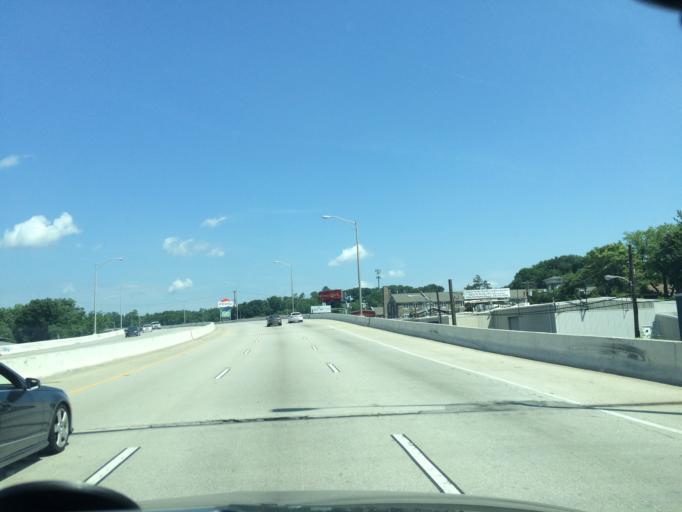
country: US
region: Maryland
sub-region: City of Baltimore
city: Baltimore
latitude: 39.3300
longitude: -76.6413
